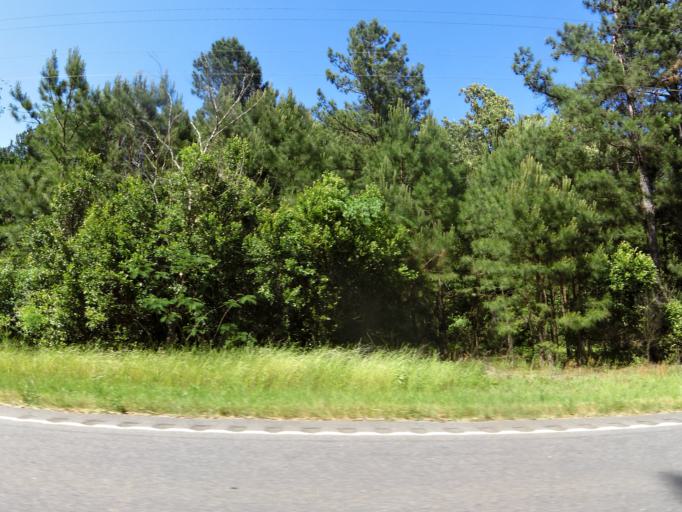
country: US
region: South Carolina
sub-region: Aiken County
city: Aiken
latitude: 33.5199
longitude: -81.6014
